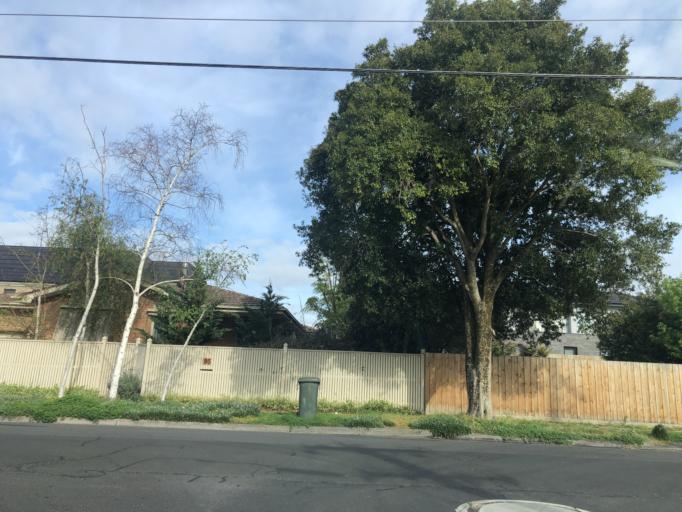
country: AU
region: Victoria
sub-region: Monash
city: Ashwood
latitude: -37.8638
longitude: 145.0987
